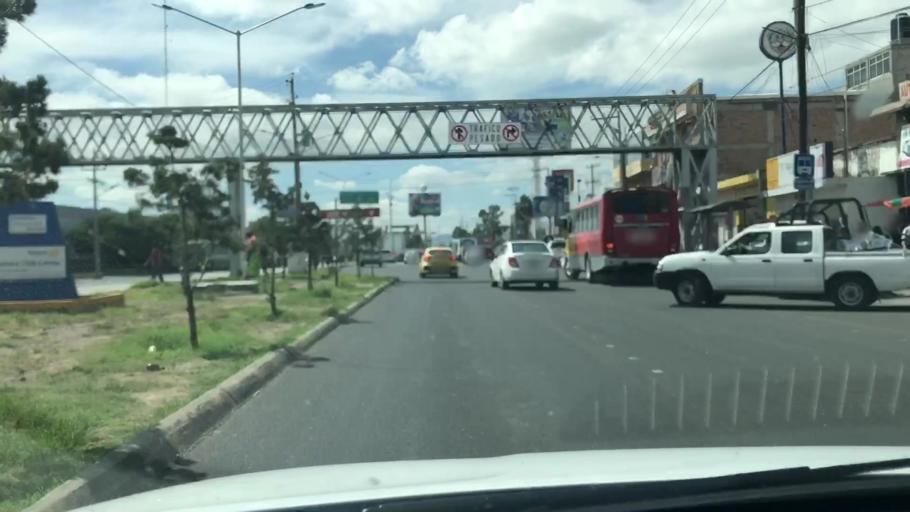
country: MX
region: Guanajuato
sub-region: Celaya
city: Roque
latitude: 20.5544
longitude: -100.8227
